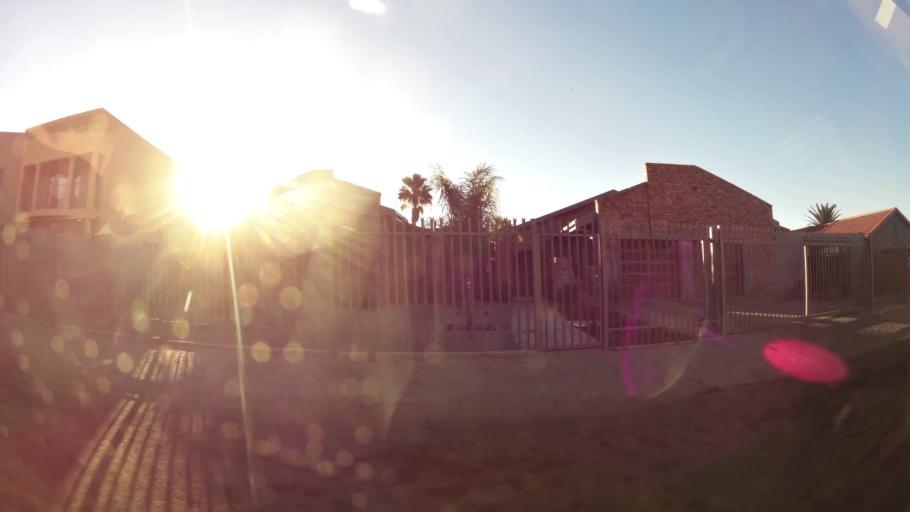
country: ZA
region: Northern Cape
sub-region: Frances Baard District Municipality
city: Kimberley
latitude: -28.7590
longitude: 24.7560
